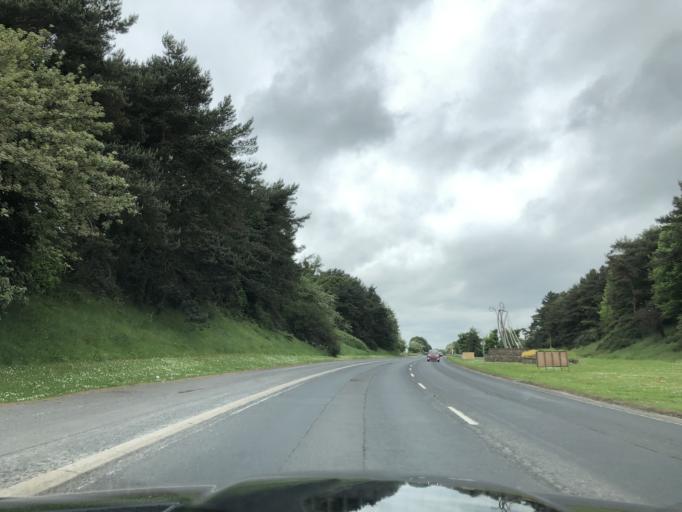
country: GB
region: Northern Ireland
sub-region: Down District
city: Downpatrick
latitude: 54.3352
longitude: -5.7209
